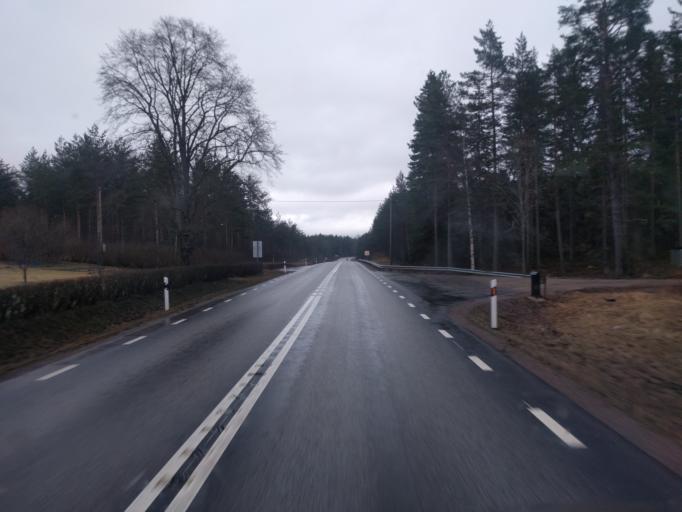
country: SE
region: Joenkoeping
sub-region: Eksjo Kommun
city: Mariannelund
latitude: 57.6148
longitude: 15.5367
